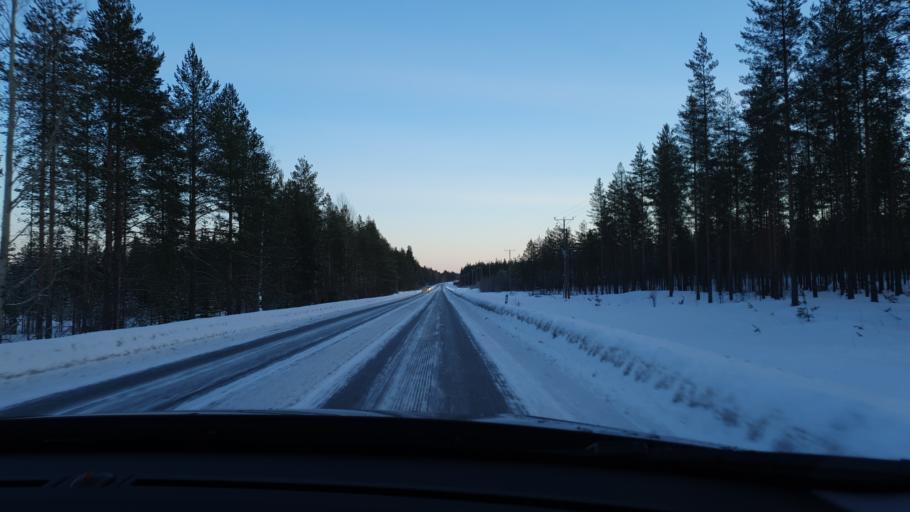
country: FI
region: Kainuu
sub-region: Kajaani
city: Sotkamo
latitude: 64.0899
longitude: 28.5689
